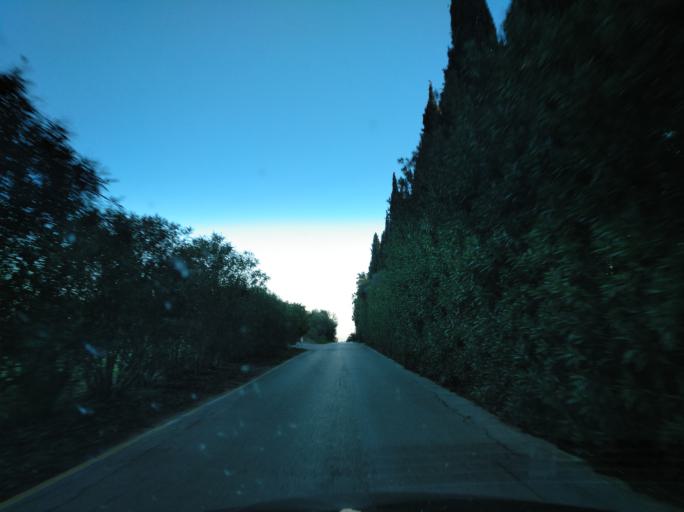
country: PT
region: Faro
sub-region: Tavira
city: Tavira
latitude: 37.1569
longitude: -7.5539
